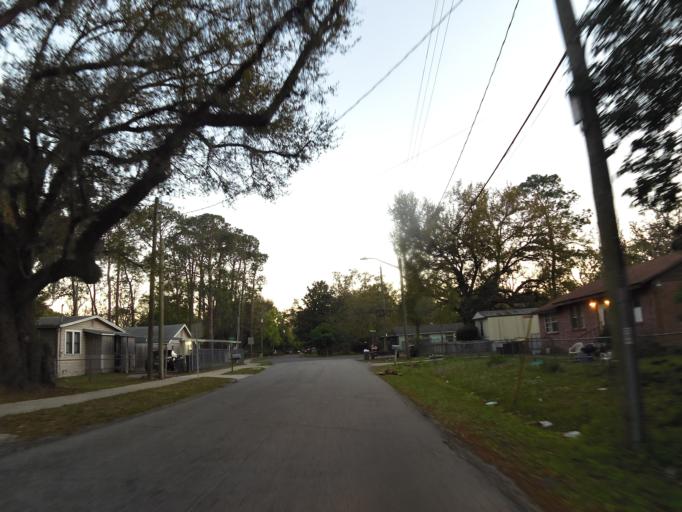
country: US
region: Florida
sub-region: Duval County
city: Jacksonville
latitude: 30.2761
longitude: -81.6310
